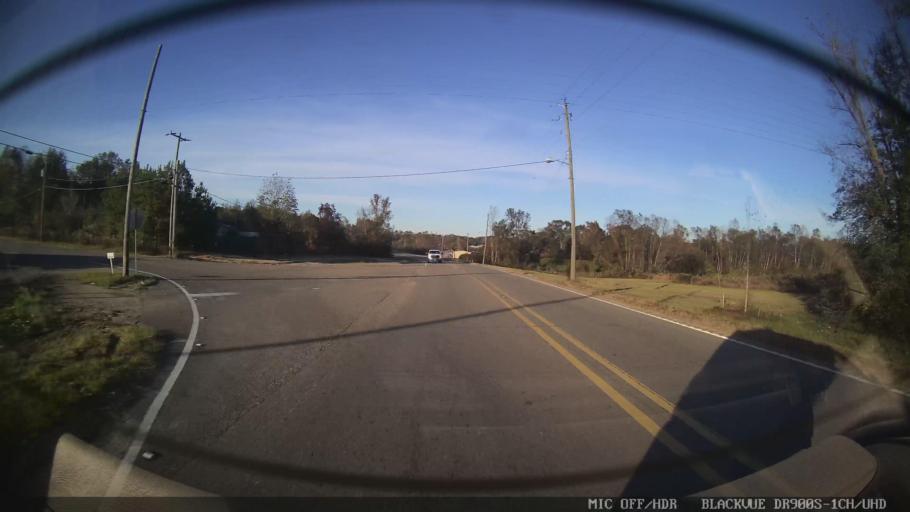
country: US
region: Mississippi
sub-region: Lamar County
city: Lumberton
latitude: 31.0046
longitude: -89.4509
